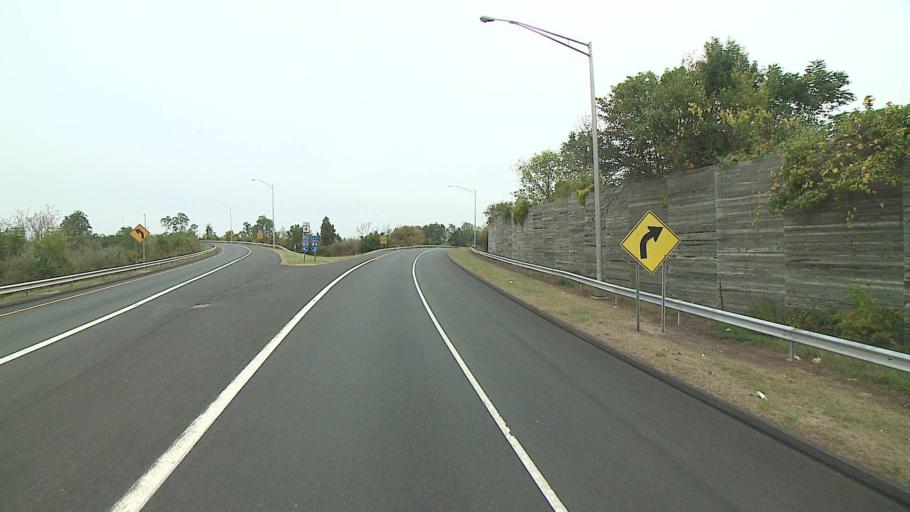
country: US
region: Connecticut
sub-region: Hartford County
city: West Hartford
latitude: 41.7241
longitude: -72.7706
